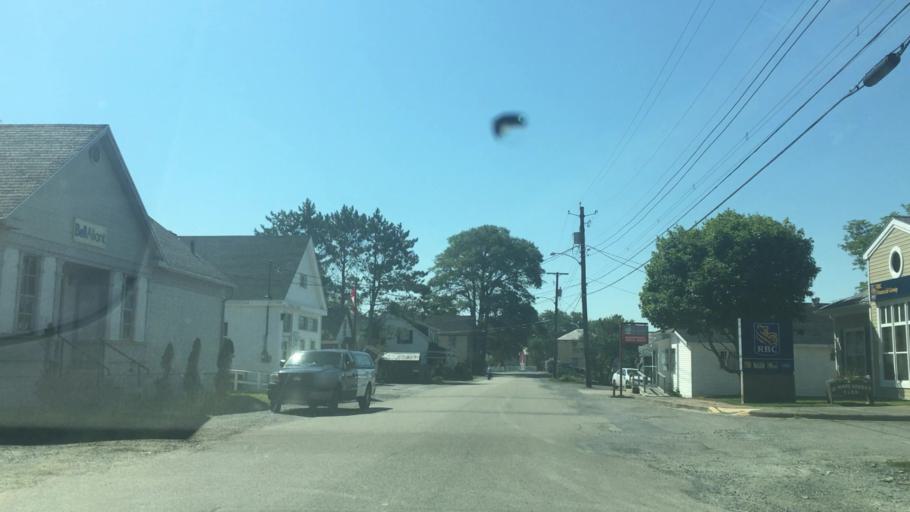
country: CA
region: Nova Scotia
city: Antigonish
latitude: 45.1423
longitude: -61.9829
